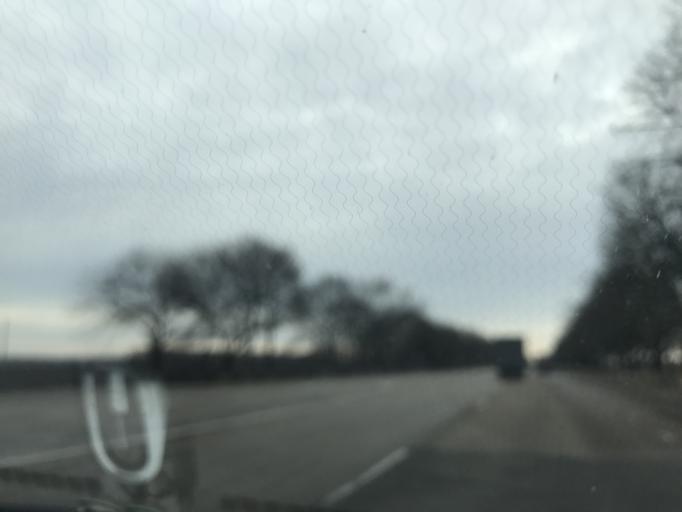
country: RU
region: Krasnodarskiy
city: Zavetnyy
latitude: 44.9492
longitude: 41.0875
